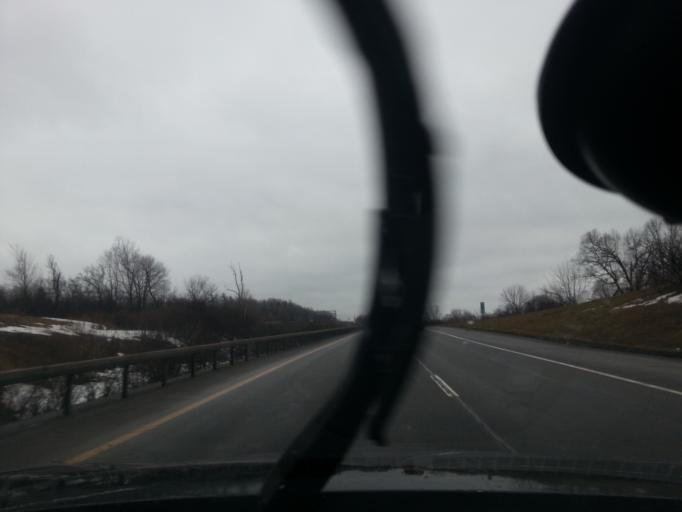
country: US
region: New York
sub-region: Onondaga County
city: Nedrow
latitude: 43.0053
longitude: -76.1347
